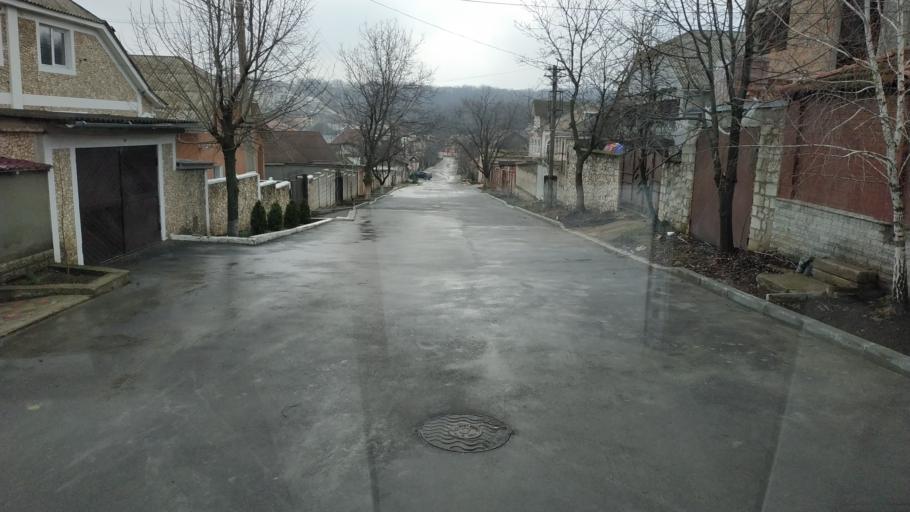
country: MD
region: Chisinau
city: Vatra
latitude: 47.0345
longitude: 28.7551
